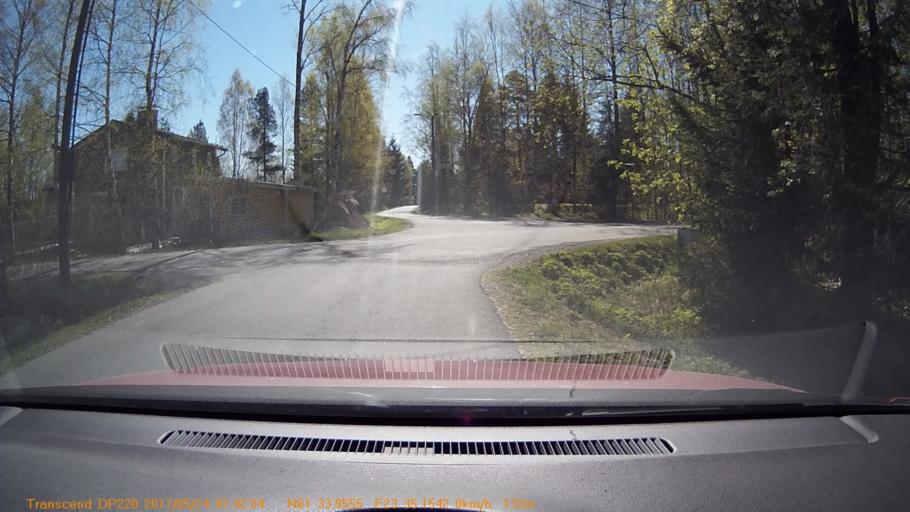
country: FI
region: Pirkanmaa
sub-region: Tampere
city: Yloejaervi
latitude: 61.5659
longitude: 23.5859
